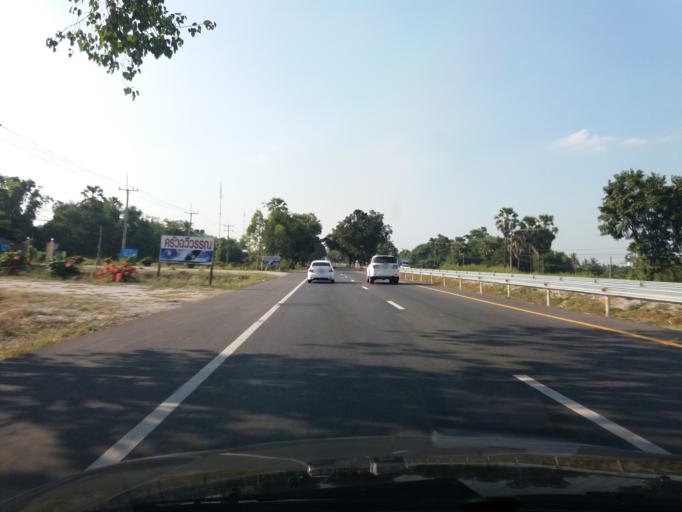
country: TH
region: Nakhon Sawan
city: Kao Liao
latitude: 15.7981
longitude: 99.9591
